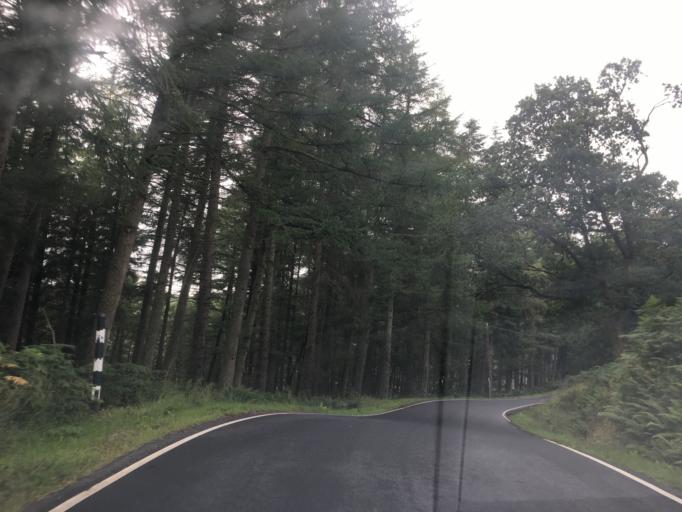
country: GB
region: Scotland
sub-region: Argyll and Bute
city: Port Bannatyne
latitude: 55.9998
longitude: -5.1145
